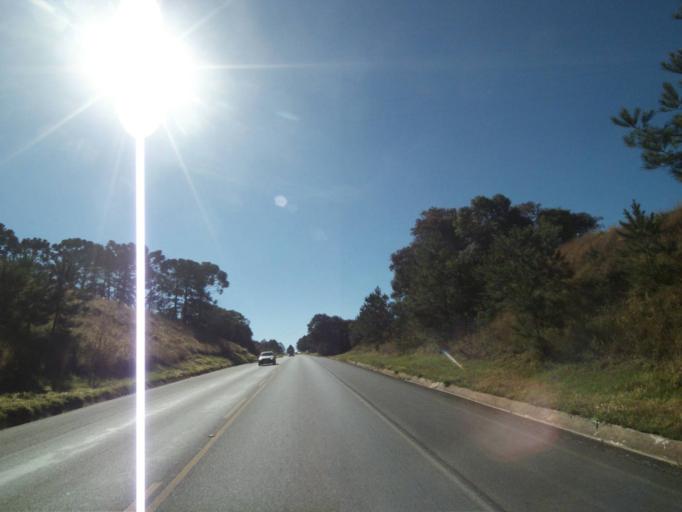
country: BR
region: Parana
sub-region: Tibagi
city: Tibagi
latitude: -24.5061
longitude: -50.4414
